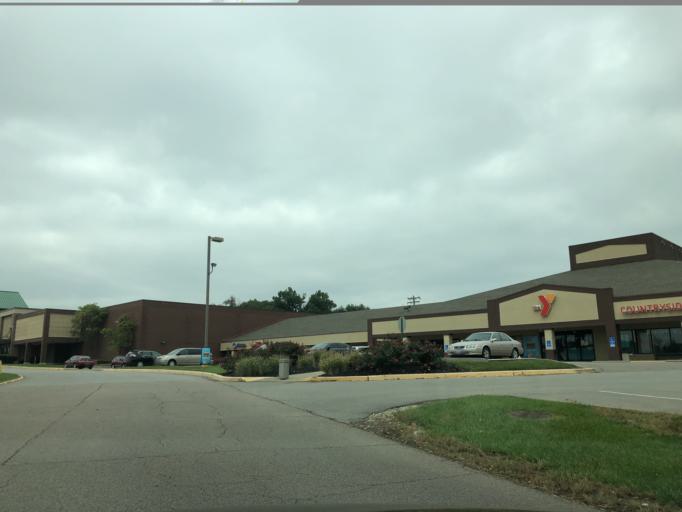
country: US
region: Ohio
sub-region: Warren County
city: Landen
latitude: 39.3110
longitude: -84.2733
